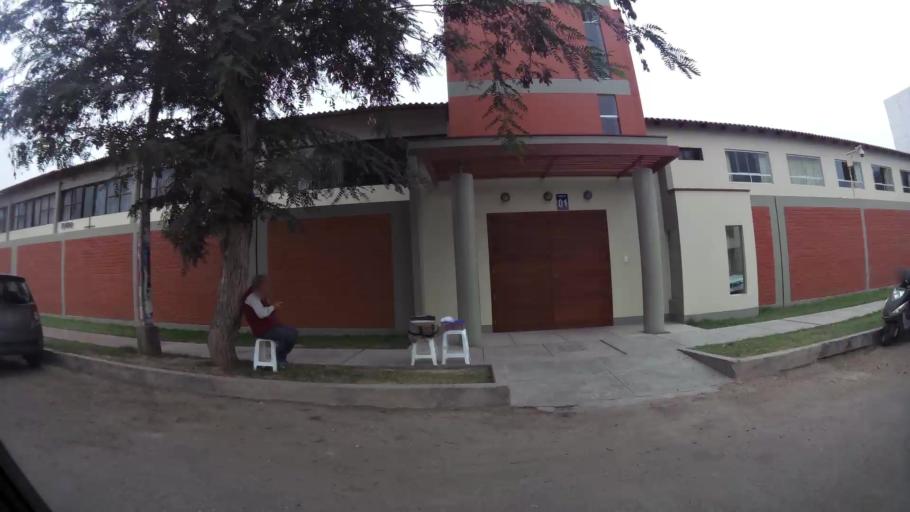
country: PE
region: La Libertad
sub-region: Provincia de Trujillo
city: Buenos Aires
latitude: -8.1316
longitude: -79.0418
